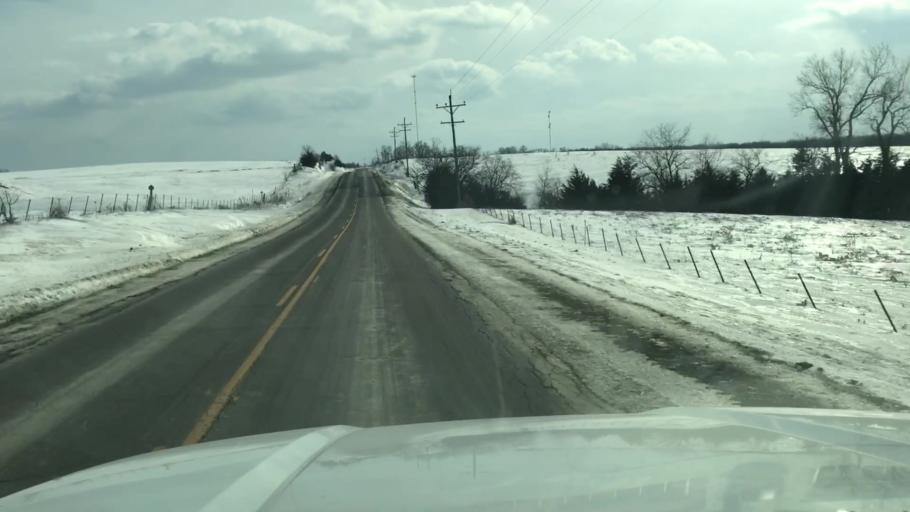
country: US
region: Missouri
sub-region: Gentry County
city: Stanberry
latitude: 40.3790
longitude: -94.6471
